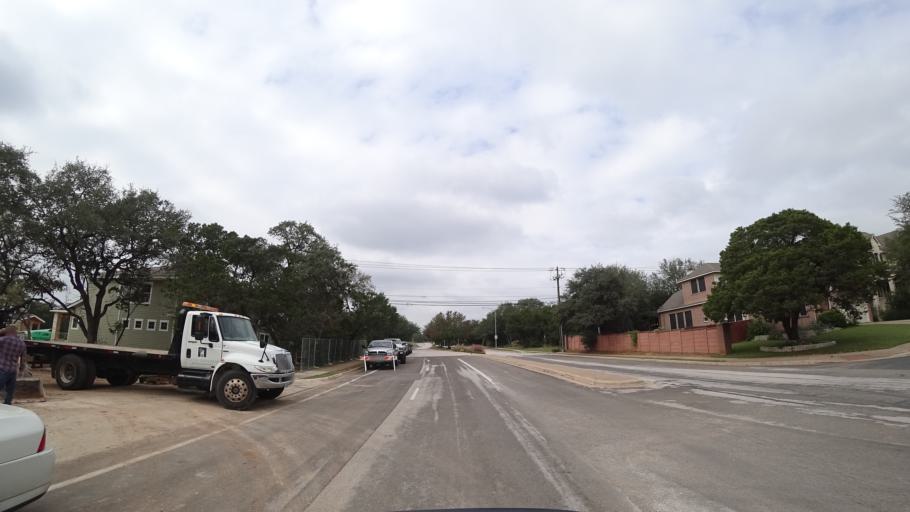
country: US
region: Texas
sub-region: Travis County
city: Shady Hollow
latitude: 30.2134
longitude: -97.8813
